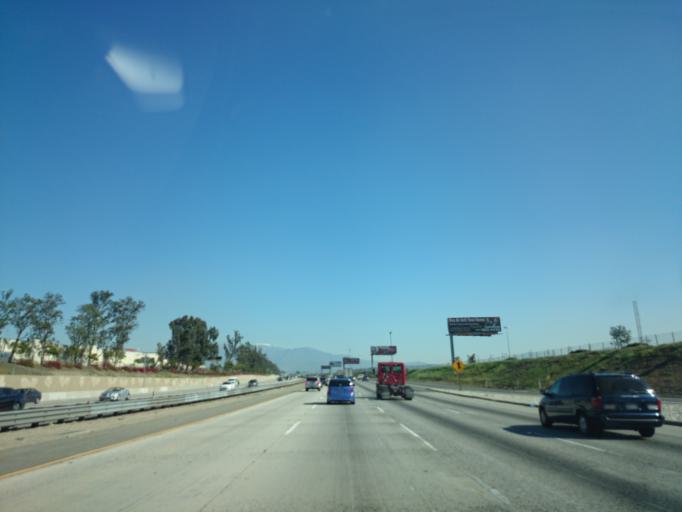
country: US
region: California
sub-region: San Bernardino County
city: Bloomington
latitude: 34.0683
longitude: -117.3921
